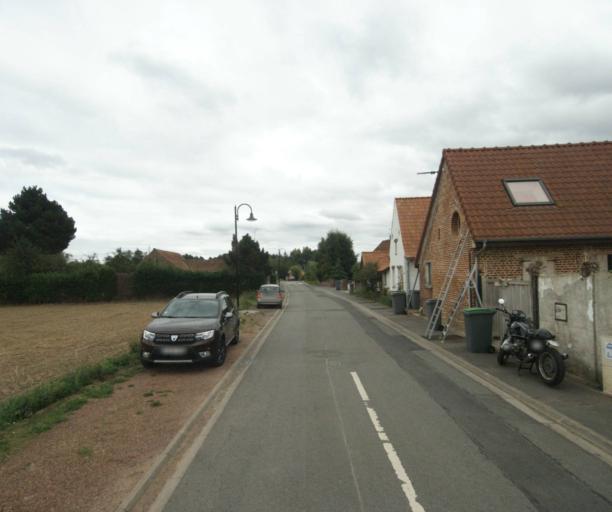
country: FR
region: Nord-Pas-de-Calais
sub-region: Departement du Nord
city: Sainghin-en-Melantois
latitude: 50.5631
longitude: 3.1728
